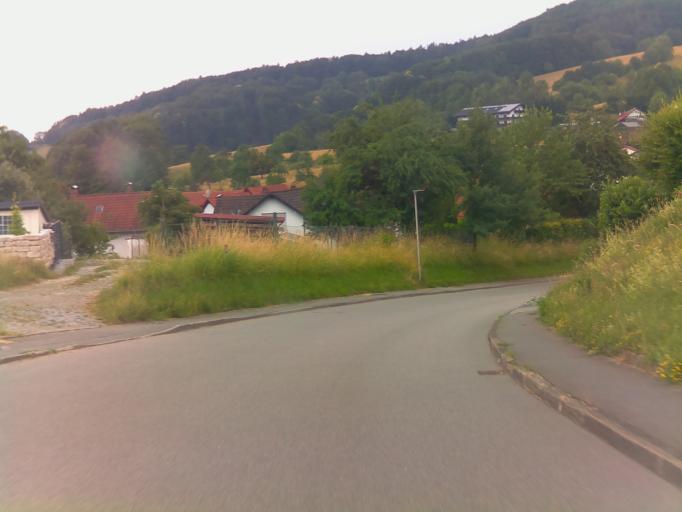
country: DE
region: Hesse
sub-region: Regierungsbezirk Darmstadt
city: Lindenfels
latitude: 49.6837
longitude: 8.7675
